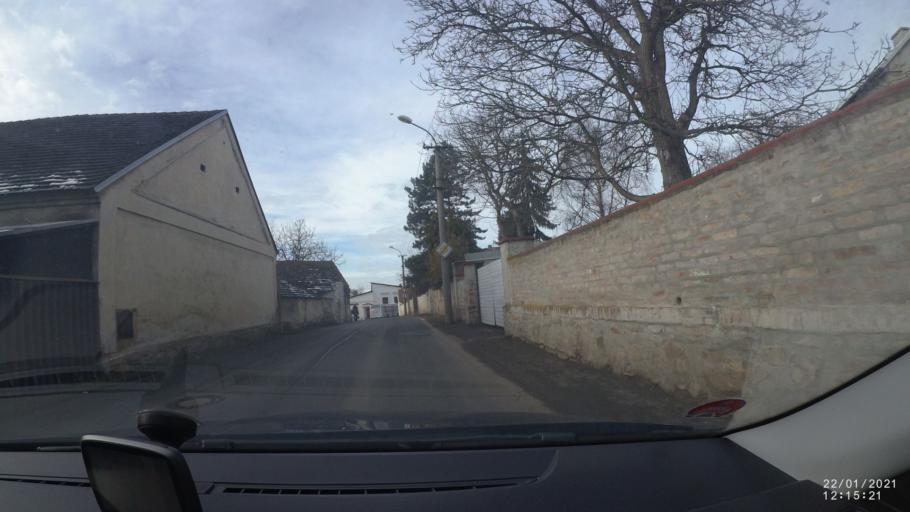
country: CZ
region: Plzensky
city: Dysina
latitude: 49.7581
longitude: 13.4599
